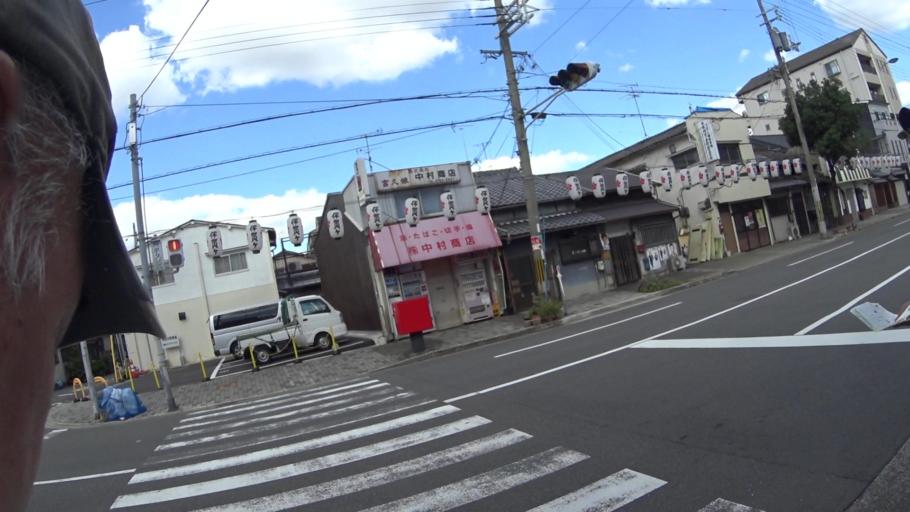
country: JP
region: Osaka
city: Yao
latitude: 34.6484
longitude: 135.5554
